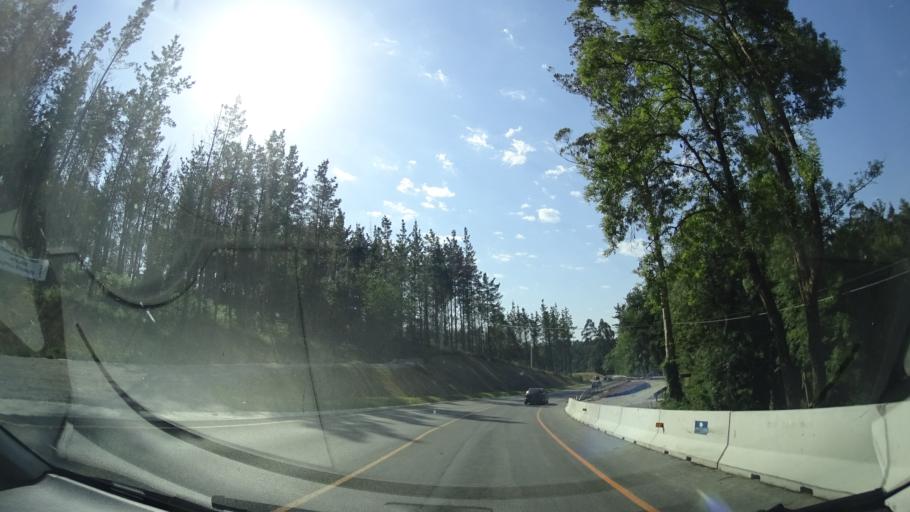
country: ES
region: Basque Country
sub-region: Bizkaia
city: Mungia
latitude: 43.3650
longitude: -2.8217
